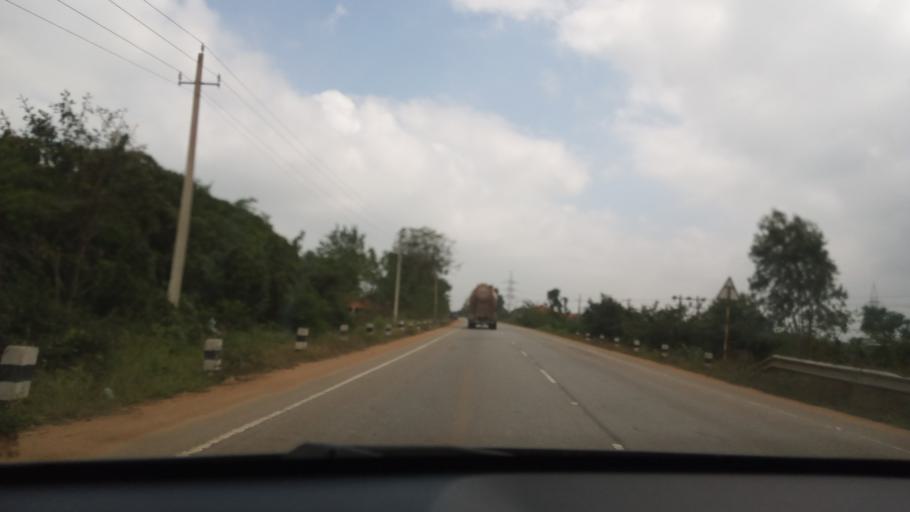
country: IN
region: Karnataka
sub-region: Chikkaballapur
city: Chintamani
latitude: 13.3686
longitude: 78.0578
